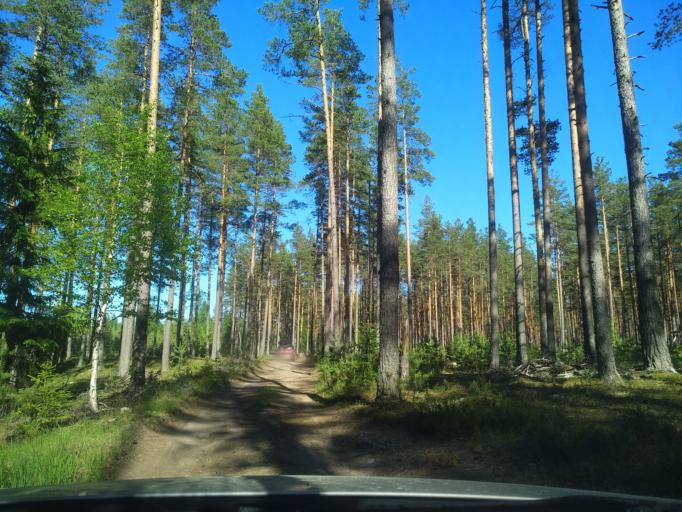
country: RU
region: Leningrad
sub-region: Vsevolzhskij Rajon
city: Vaskelovo
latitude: 60.5140
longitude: 30.4808
